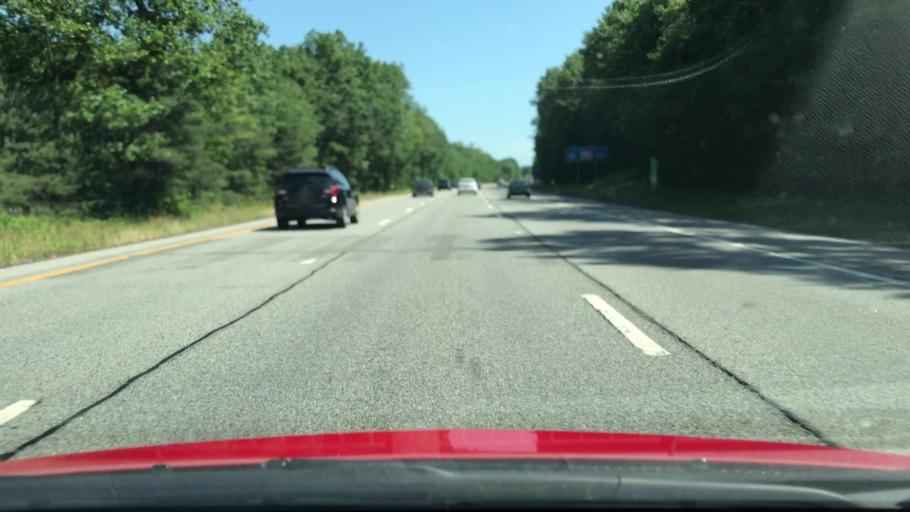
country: US
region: New York
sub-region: Saratoga County
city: Saratoga Springs
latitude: 43.1575
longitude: -73.7215
